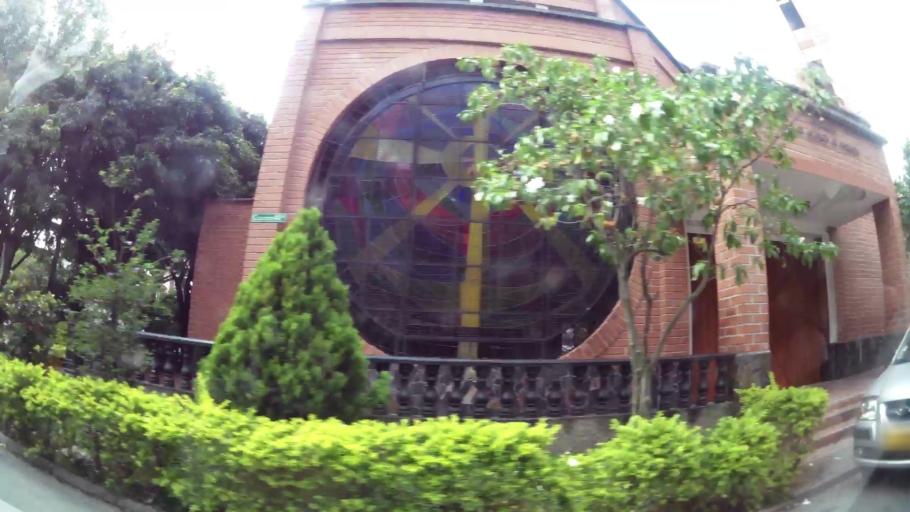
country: CO
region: Antioquia
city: Envigado
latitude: 6.1596
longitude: -75.5941
